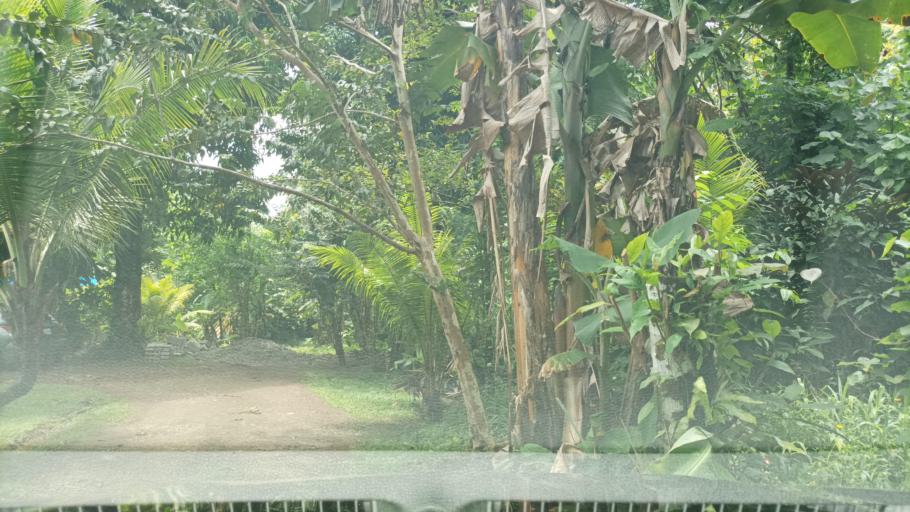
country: FM
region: Pohnpei
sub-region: Kolonia Municipality
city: Kolonia
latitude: 6.9651
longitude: 158.2221
